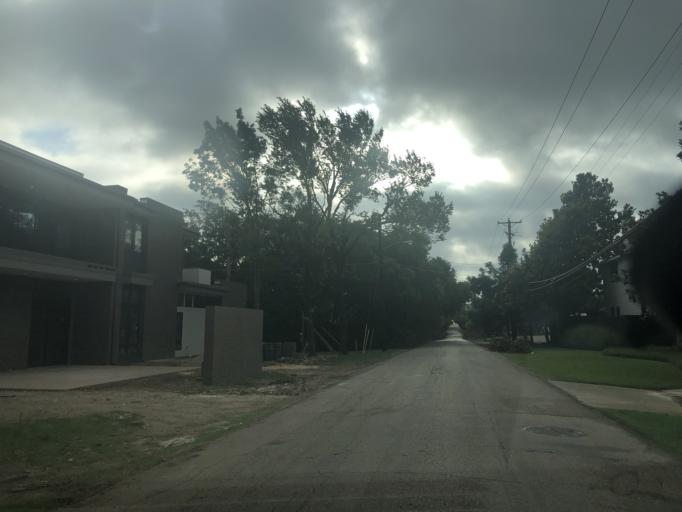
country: US
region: Texas
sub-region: Dallas County
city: University Park
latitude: 32.8558
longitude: -96.8456
